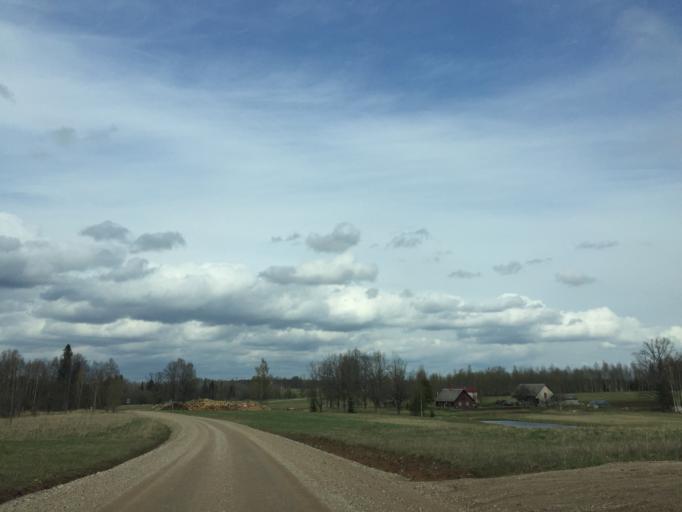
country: LV
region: Ligatne
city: Ligatne
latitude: 57.2062
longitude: 25.0594
